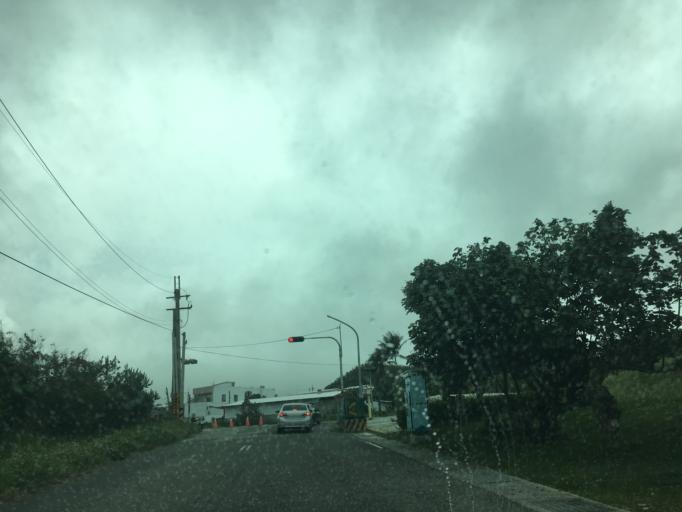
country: TW
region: Taiwan
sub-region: Taitung
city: Taitung
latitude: 22.7933
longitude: 121.1935
